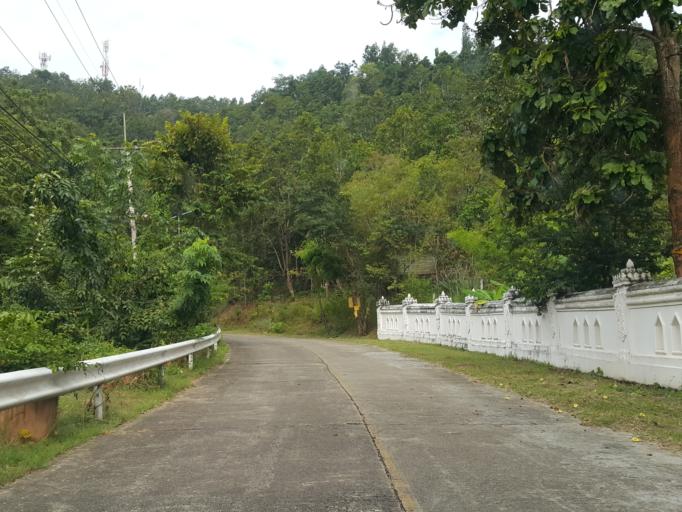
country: TH
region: Mae Hong Son
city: Mae Hong Son
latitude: 19.2984
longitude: 97.9626
